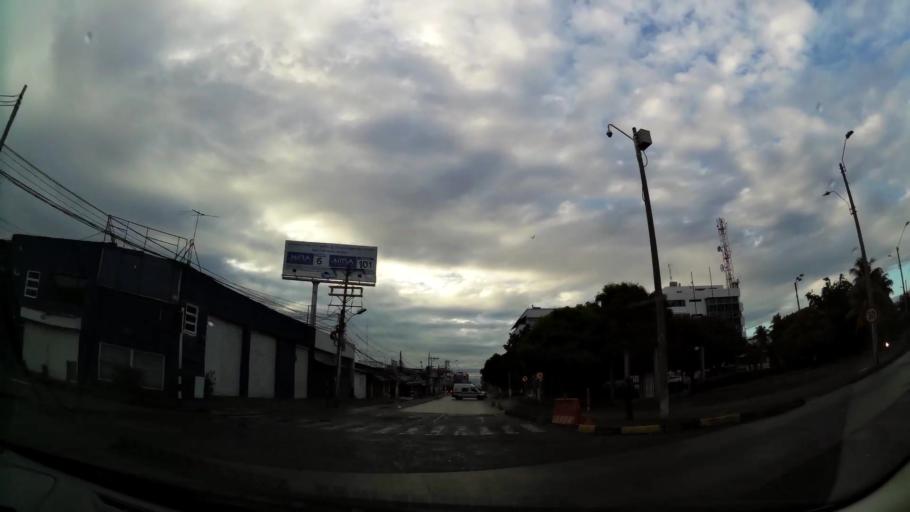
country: CO
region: Valle del Cauca
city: Cali
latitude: 3.4596
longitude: -76.5266
